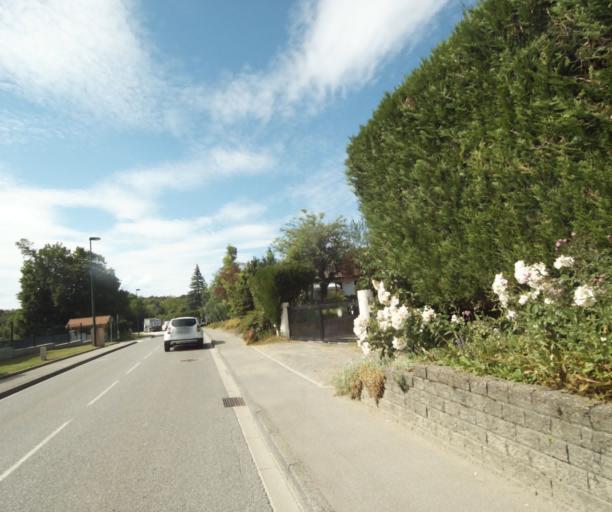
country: FR
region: Rhone-Alpes
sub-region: Departement de la Haute-Savoie
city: Allinges
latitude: 46.3405
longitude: 6.4782
